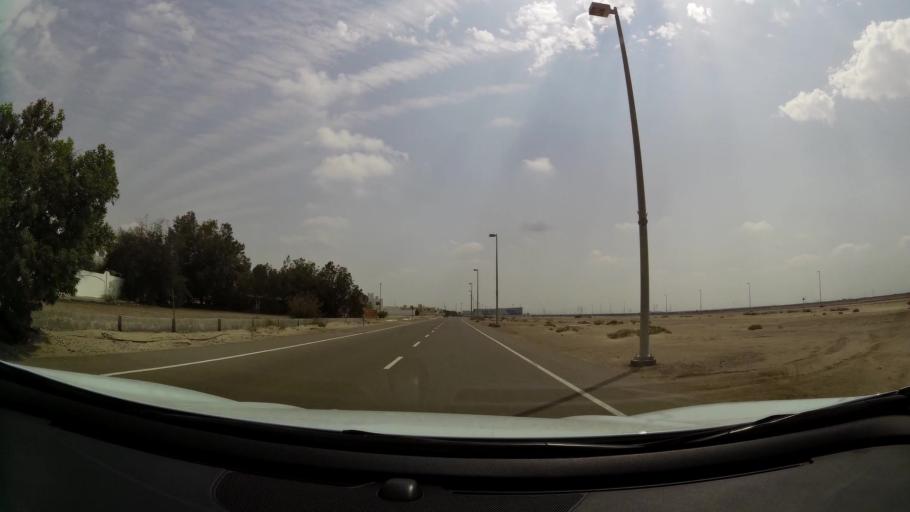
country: AE
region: Abu Dhabi
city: Abu Dhabi
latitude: 24.5429
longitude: 54.6234
